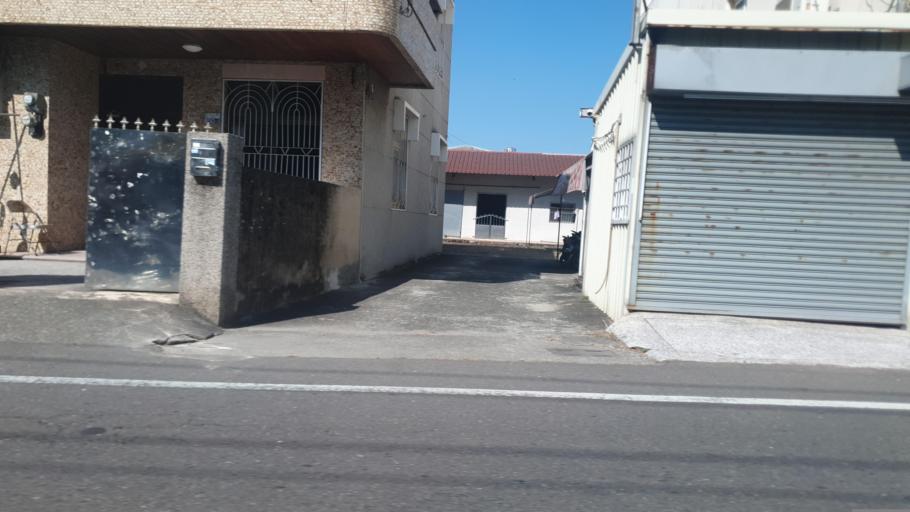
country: TW
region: Taiwan
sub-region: Tainan
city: Tainan
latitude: 23.0293
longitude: 120.2943
